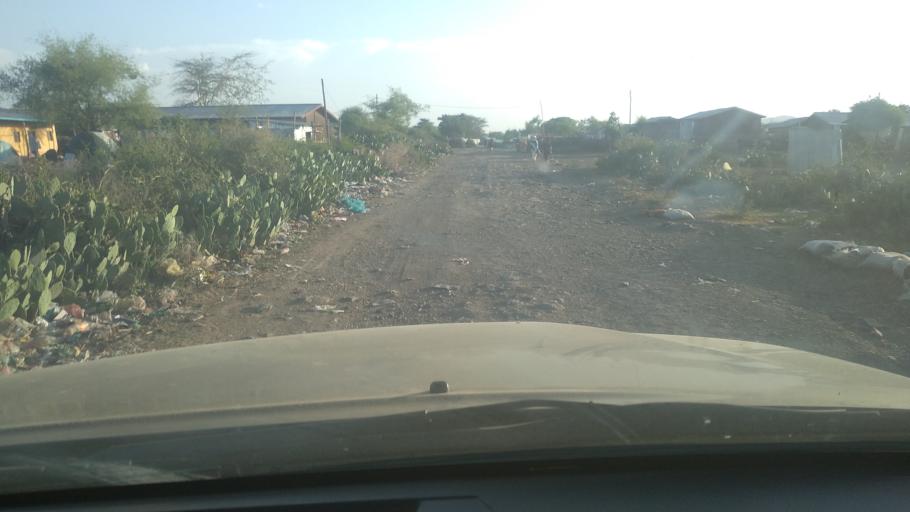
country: ET
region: Oromiya
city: Asbe Teferi
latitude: 9.2959
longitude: 40.8377
